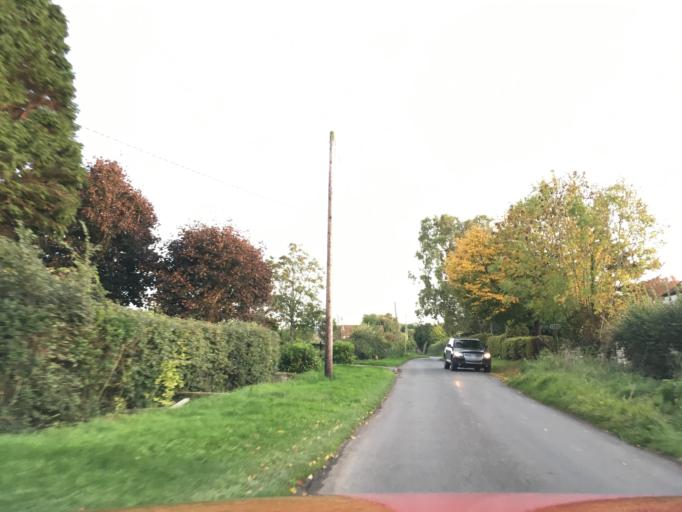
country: GB
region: England
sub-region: South Gloucestershire
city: Thornbury
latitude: 51.6203
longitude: -2.5476
